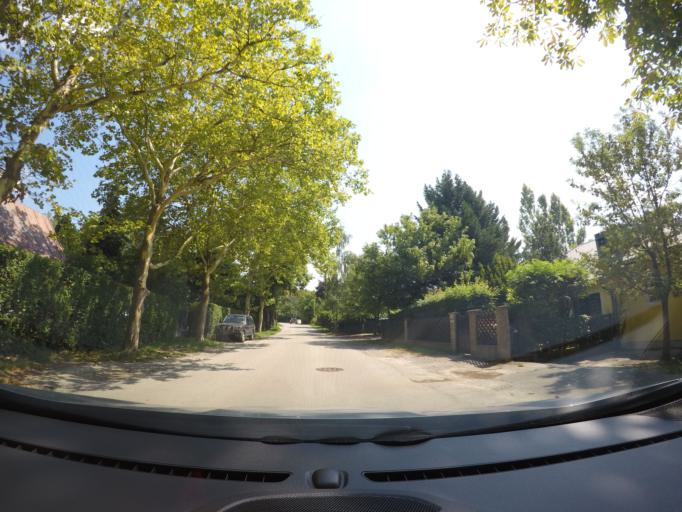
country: AT
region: Lower Austria
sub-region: Politischer Bezirk Tulln
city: Konigstetten
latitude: 48.2725
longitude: 16.1536
